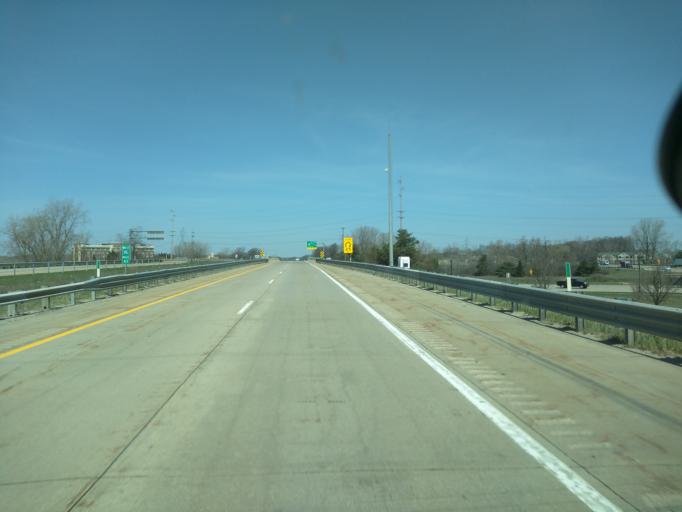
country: US
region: Michigan
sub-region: Kent County
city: Forest Hills
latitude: 42.9118
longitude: -85.5343
